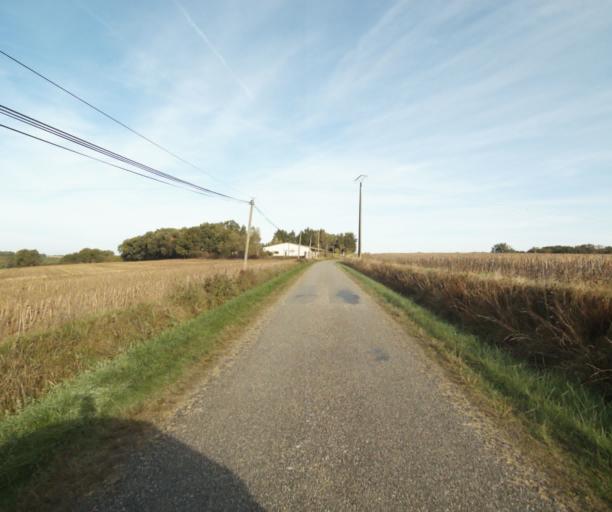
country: FR
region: Midi-Pyrenees
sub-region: Departement de la Haute-Garonne
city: Villemur-sur-Tarn
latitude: 43.9030
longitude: 1.5166
